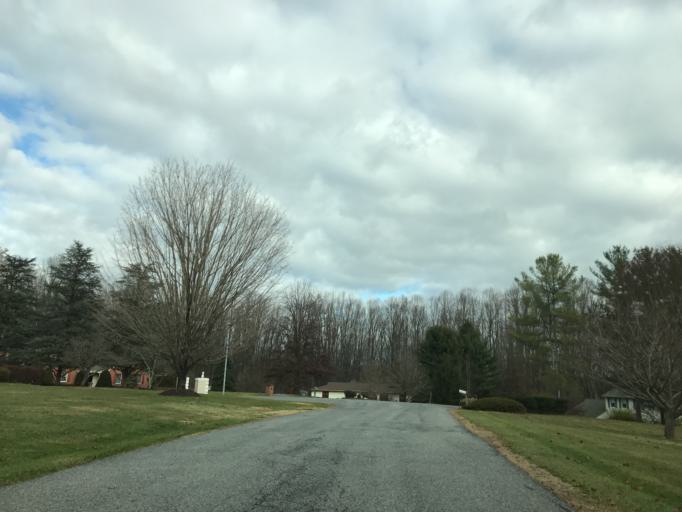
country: US
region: Maryland
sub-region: Harford County
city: Fallston
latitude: 39.5130
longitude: -76.4751
